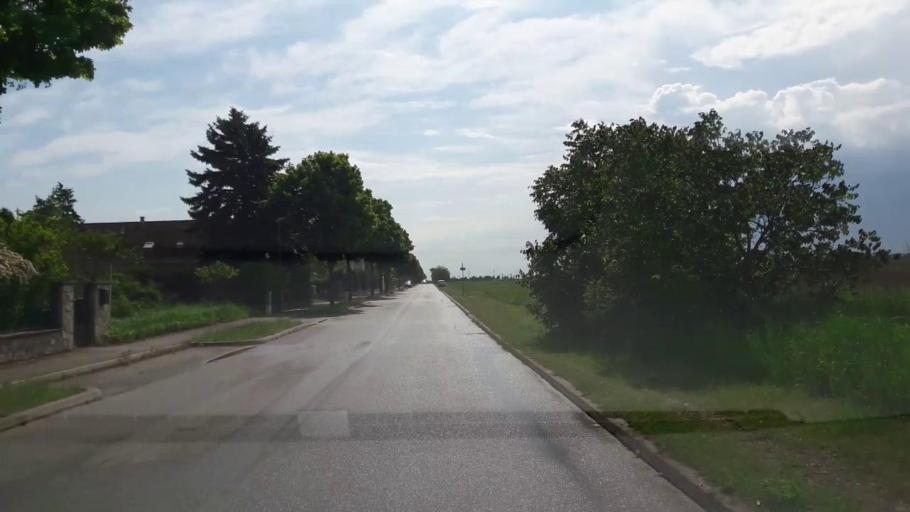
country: AT
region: Lower Austria
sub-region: Politischer Bezirk Ganserndorf
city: Deutsch-Wagram
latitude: 48.3140
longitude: 16.5899
